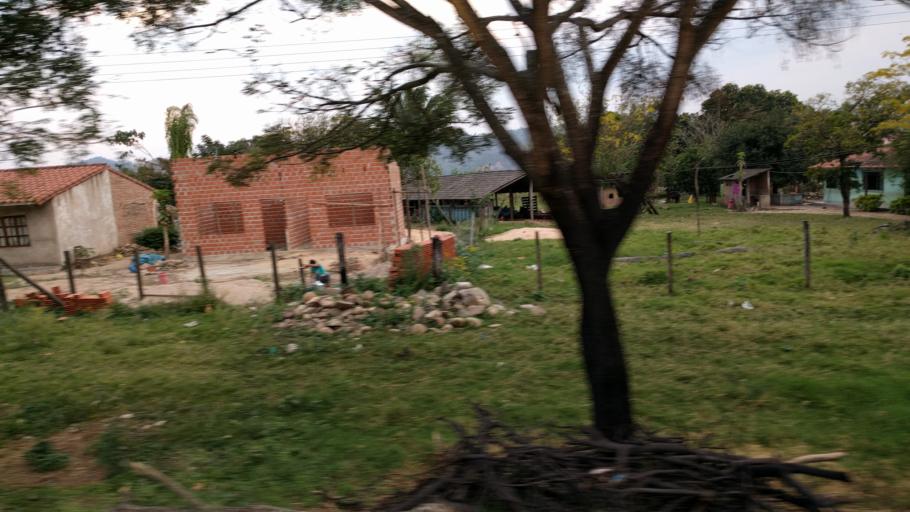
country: BO
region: Santa Cruz
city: Jorochito
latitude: -18.1353
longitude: -63.4739
